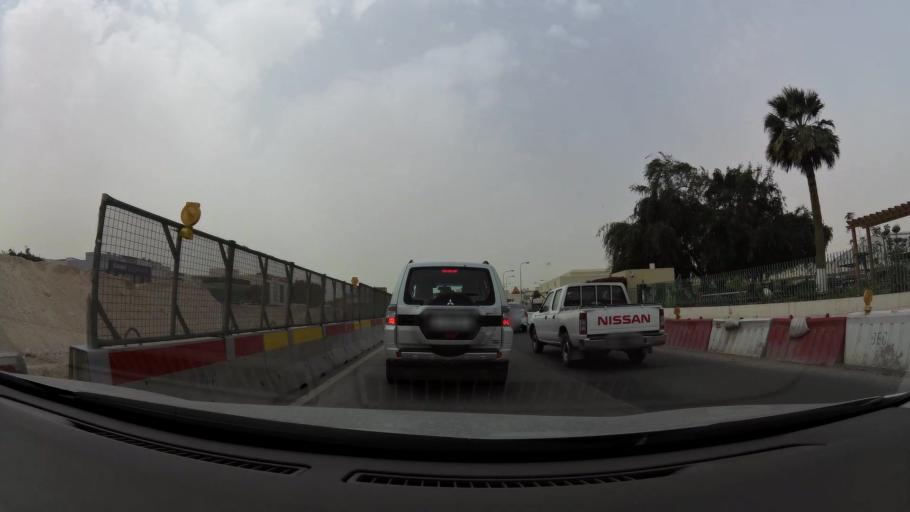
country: QA
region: Baladiyat ad Dawhah
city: Doha
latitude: 25.2636
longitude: 51.5066
